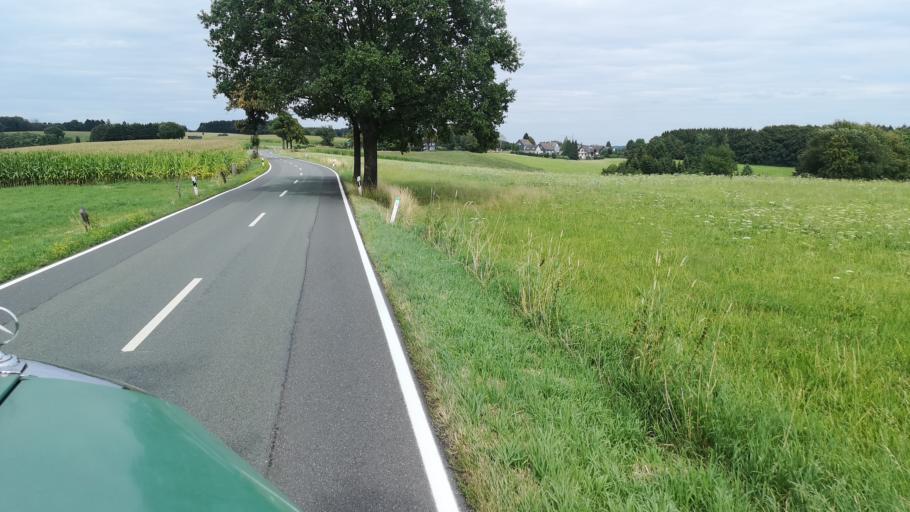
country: DE
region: North Rhine-Westphalia
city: Wermelskirchen
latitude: 51.1295
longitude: 7.2653
